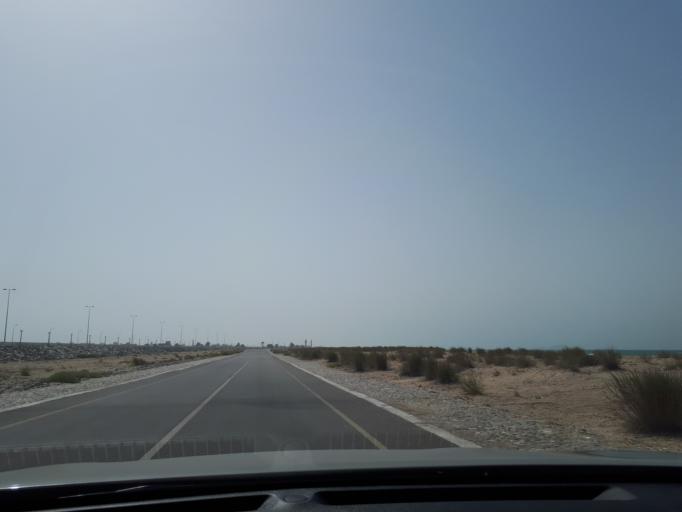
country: OM
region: Al Batinah
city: Barka'
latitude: 23.7160
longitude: 57.8659
